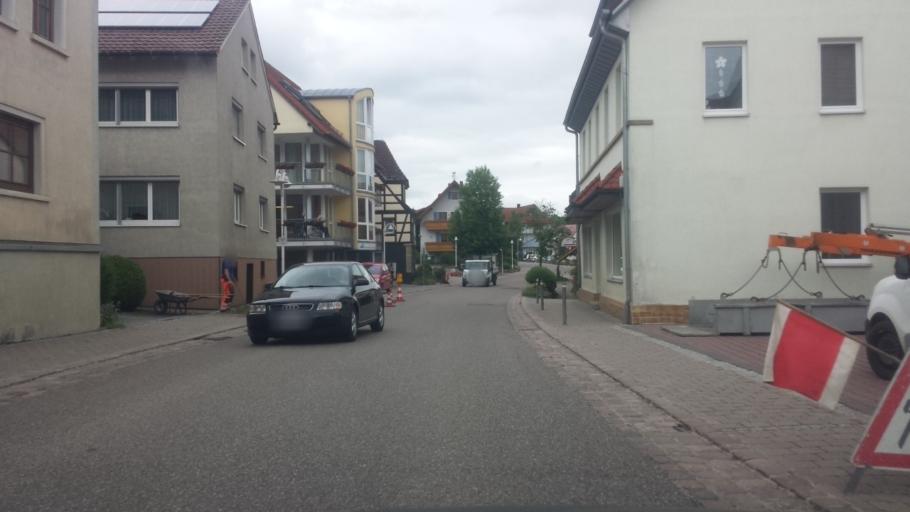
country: DE
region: Baden-Wuerttemberg
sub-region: Regierungsbezirk Stuttgart
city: Rot am See
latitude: 49.2497
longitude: 10.0255
